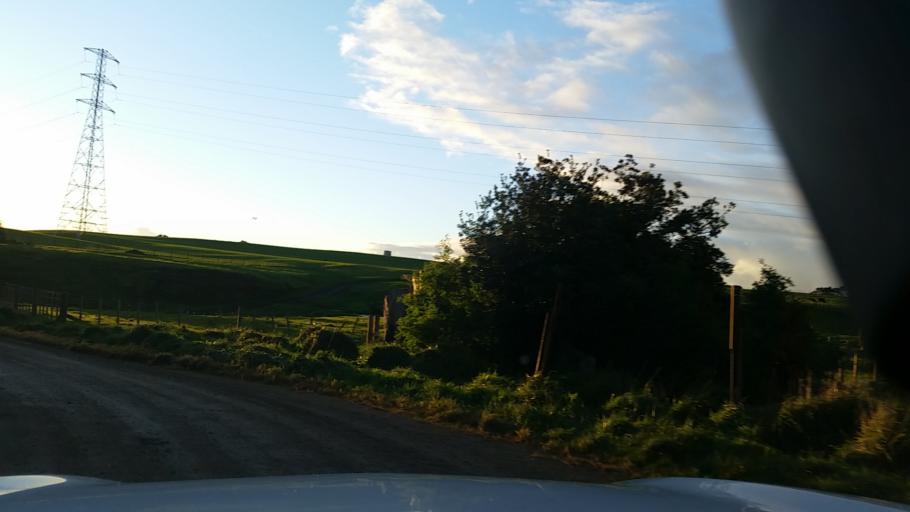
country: NZ
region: Manawatu-Wanganui
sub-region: Wanganui District
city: Wanganui
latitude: -39.8011
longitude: 174.8042
